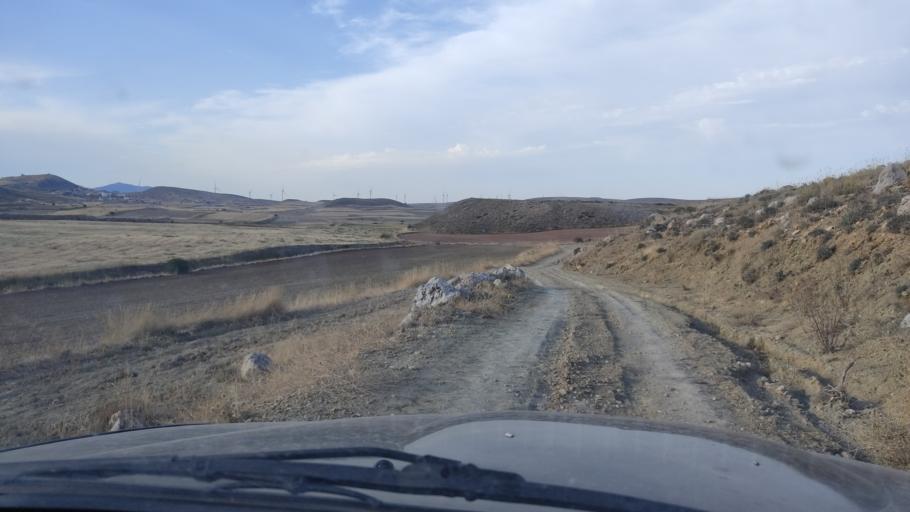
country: ES
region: Aragon
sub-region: Provincia de Teruel
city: Monforte de Moyuela
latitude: 41.0355
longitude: -0.9980
